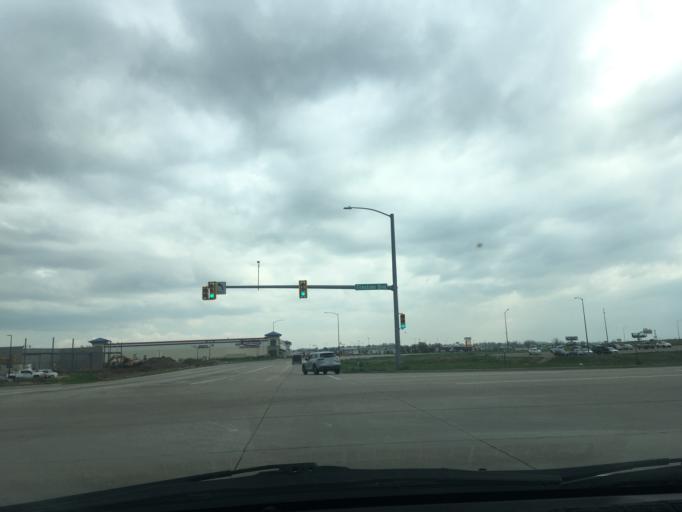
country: US
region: Colorado
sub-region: Weld County
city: Firestone
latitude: 40.1608
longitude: -104.9755
